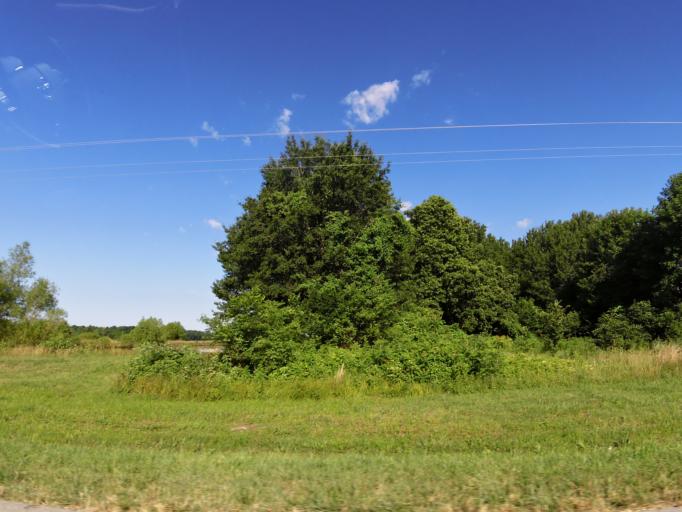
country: US
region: Arkansas
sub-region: Clay County
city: Corning
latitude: 36.5728
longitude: -90.5208
